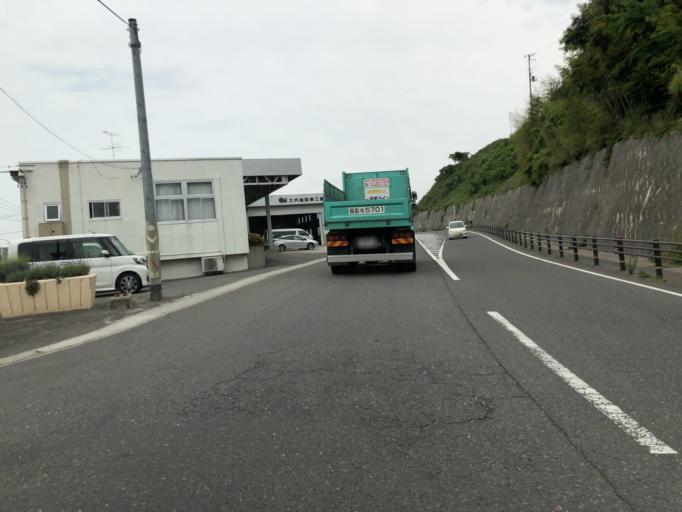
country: JP
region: Fukushima
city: Funehikimachi-funehiki
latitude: 37.4348
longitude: 140.5872
